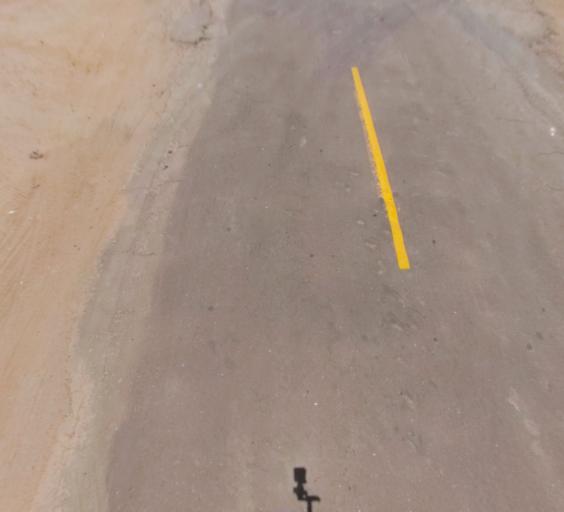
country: US
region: California
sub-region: Fresno County
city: Clovis
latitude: 36.8702
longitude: -119.8205
